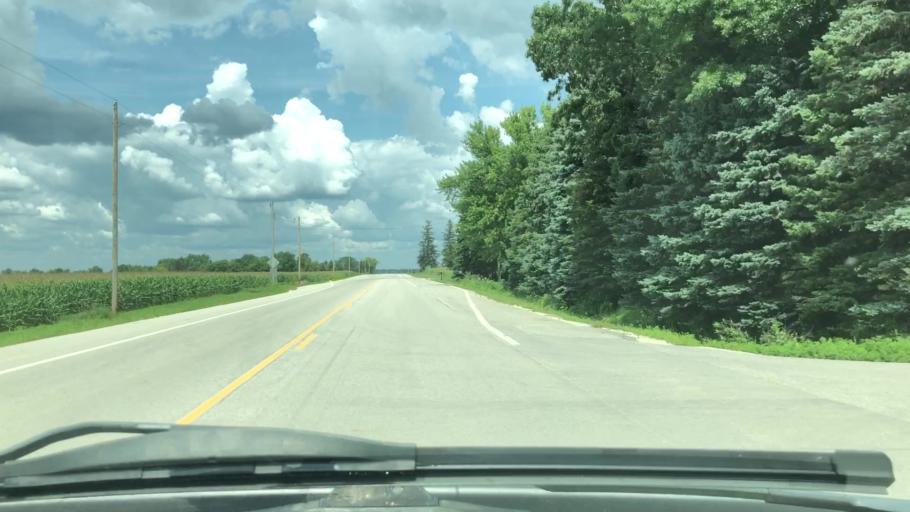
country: US
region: Minnesota
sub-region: Olmsted County
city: Rochester
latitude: 43.9517
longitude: -92.5184
